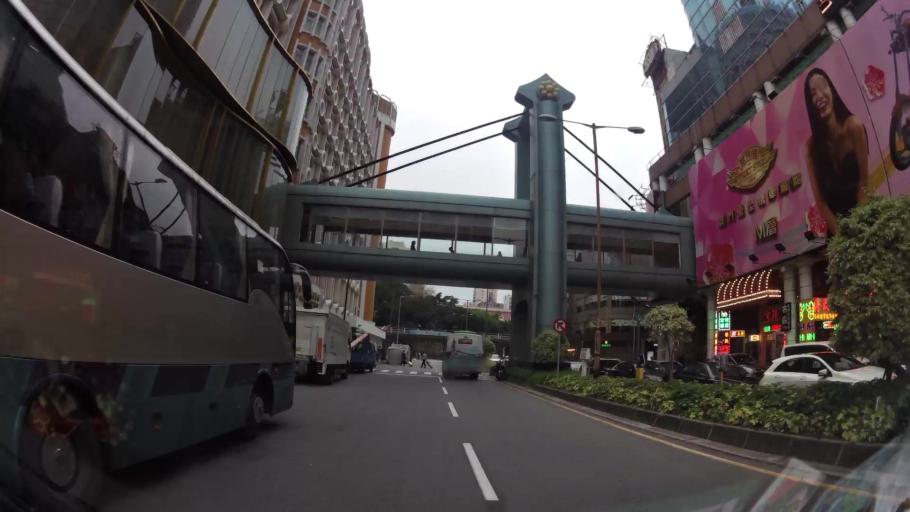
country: MO
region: Macau
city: Macau
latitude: 22.1900
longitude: 113.5455
